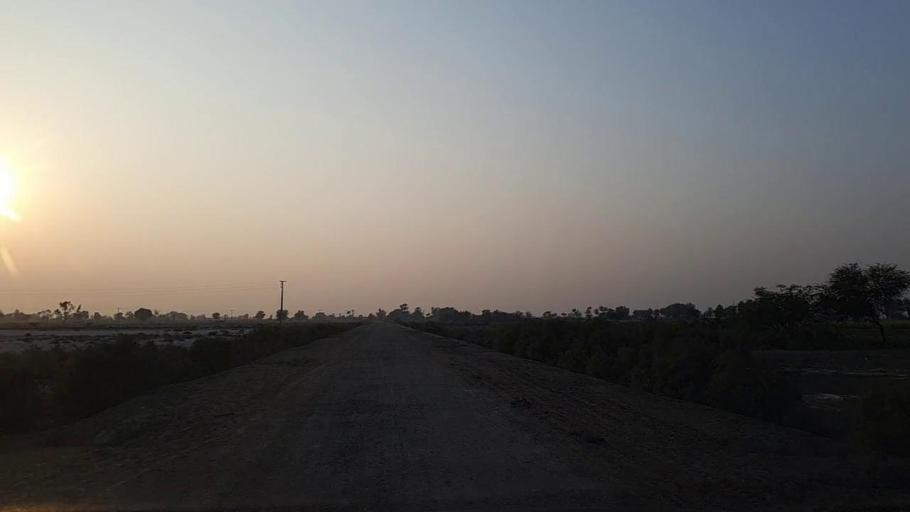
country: PK
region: Sindh
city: Daur
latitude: 26.4168
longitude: 68.3644
